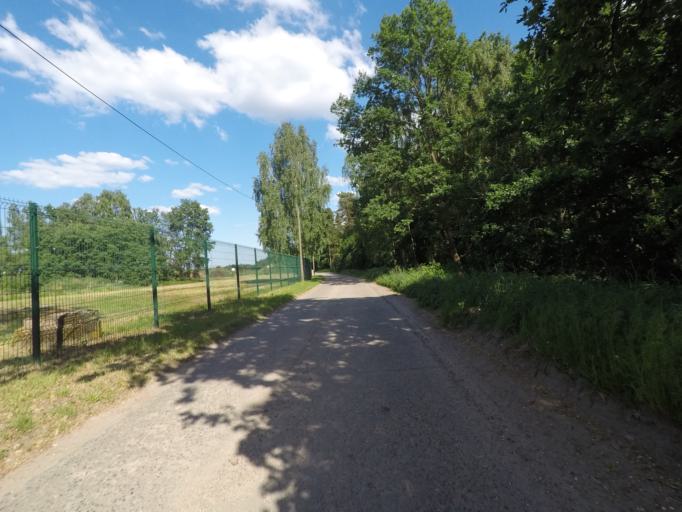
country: DE
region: Brandenburg
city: Britz
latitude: 52.8685
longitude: 13.7767
